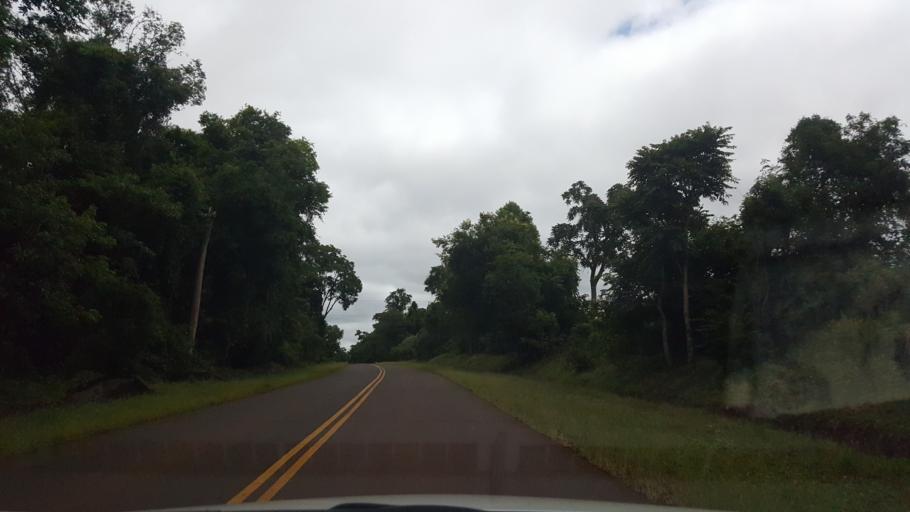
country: AR
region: Misiones
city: Ruiz de Montoya
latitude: -26.9656
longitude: -55.0884
